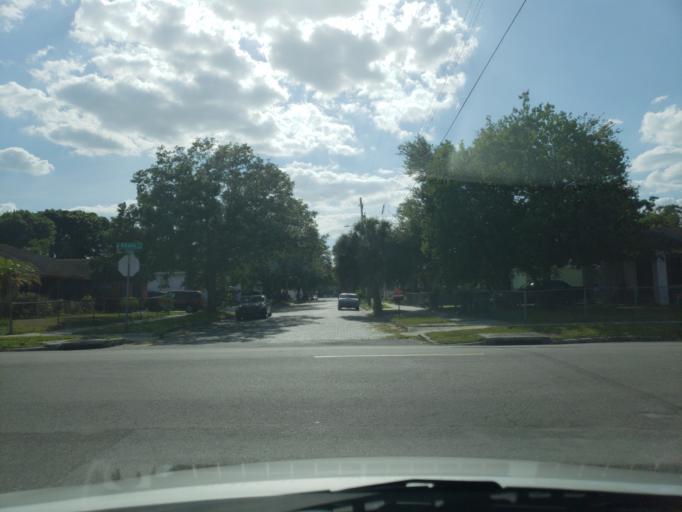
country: US
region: Florida
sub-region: Hillsborough County
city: Tampa
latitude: 27.9616
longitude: -82.4807
